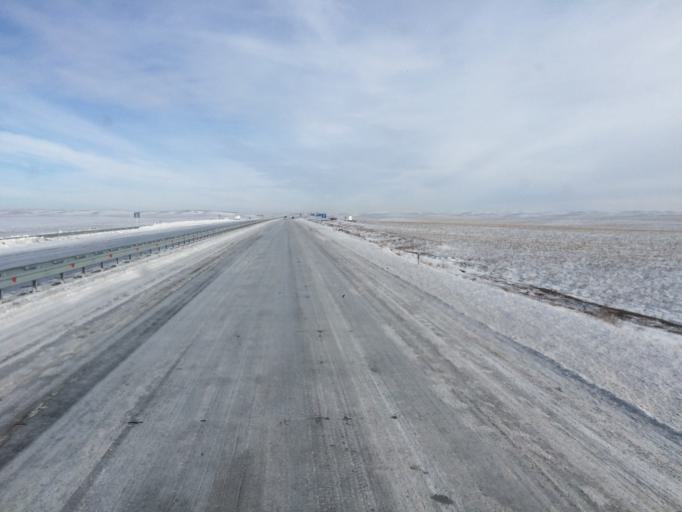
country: KZ
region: Zhambyl
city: Georgiyevka
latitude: 43.3584
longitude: 74.6102
